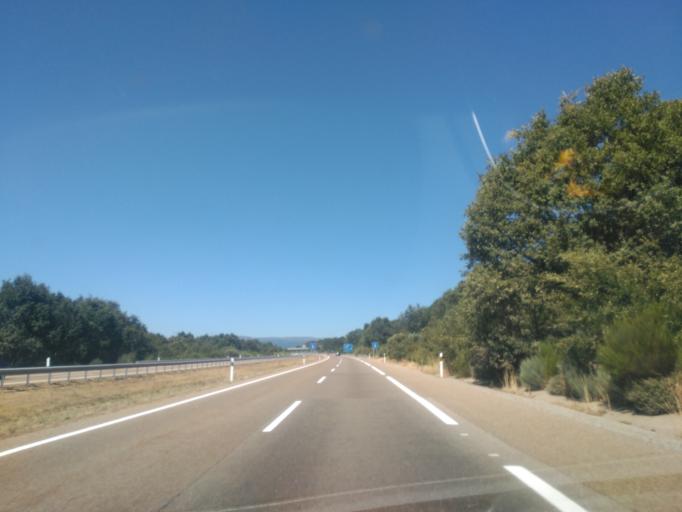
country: ES
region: Castille and Leon
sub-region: Provincia de Zamora
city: Palacios de Sanabria
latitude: 42.0506
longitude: -6.5368
